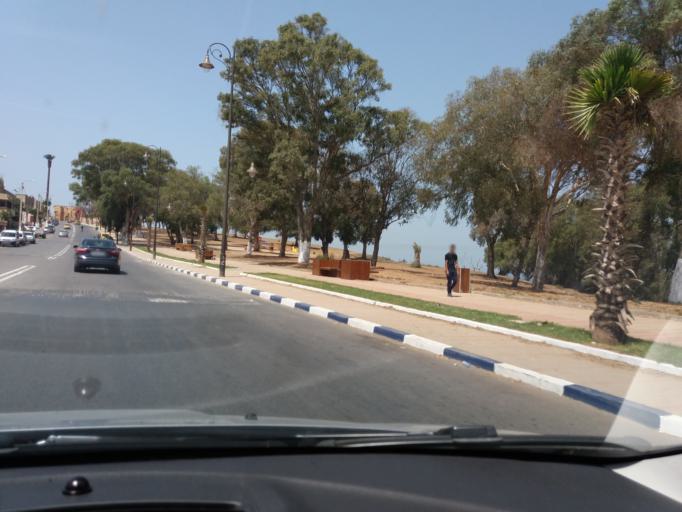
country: MA
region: Gharb-Chrarda-Beni Hssen
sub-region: Kenitra Province
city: Kenitra
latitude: 34.2650
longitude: -6.6523
